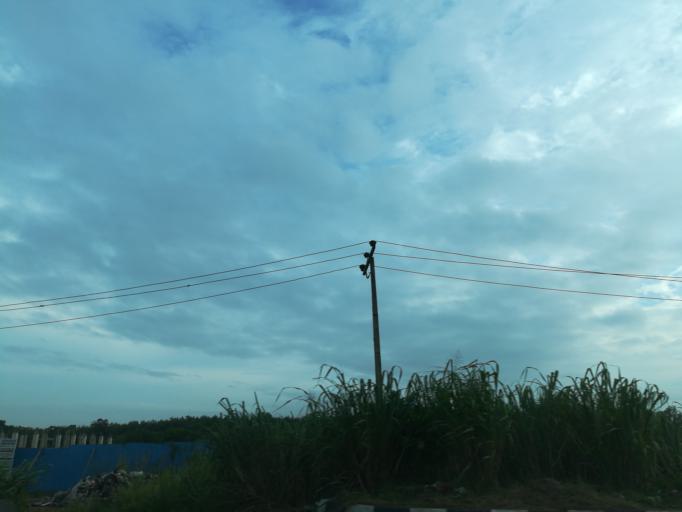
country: NG
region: Lagos
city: Ebute Ikorodu
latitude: 6.6185
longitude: 3.4606
